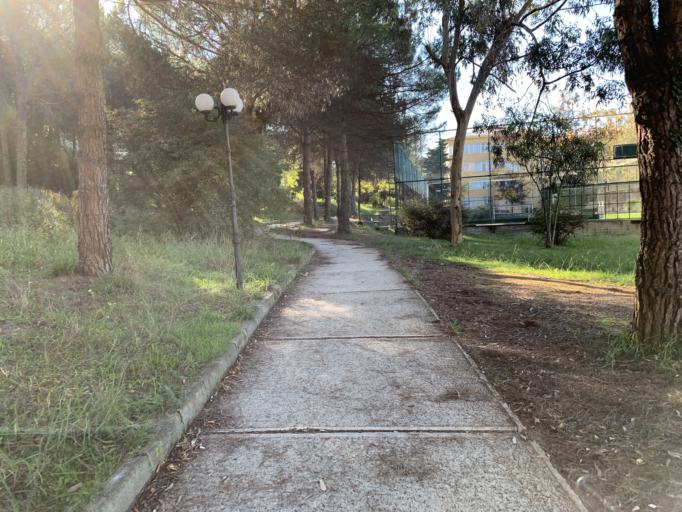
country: TR
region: Trabzon
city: Trabzon
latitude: 40.9960
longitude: 39.7712
